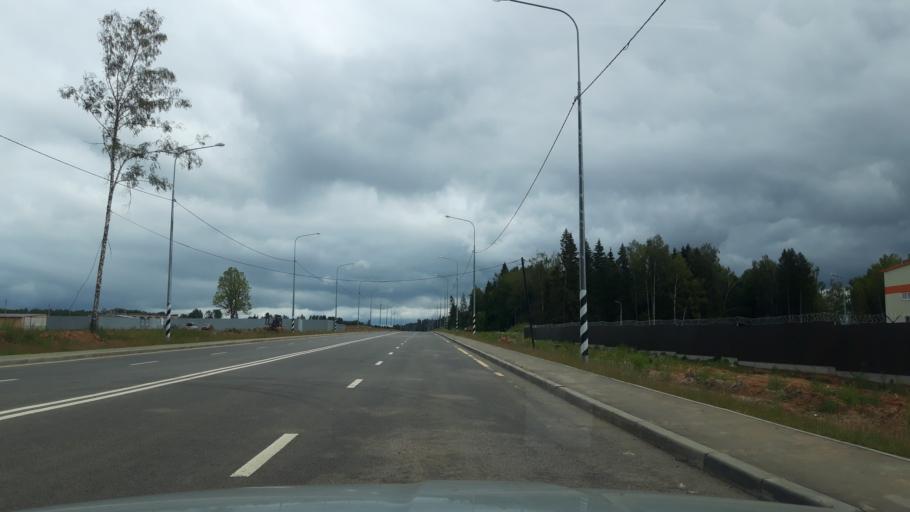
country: RU
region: Moskovskaya
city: Lozhki
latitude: 56.0802
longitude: 37.0940
